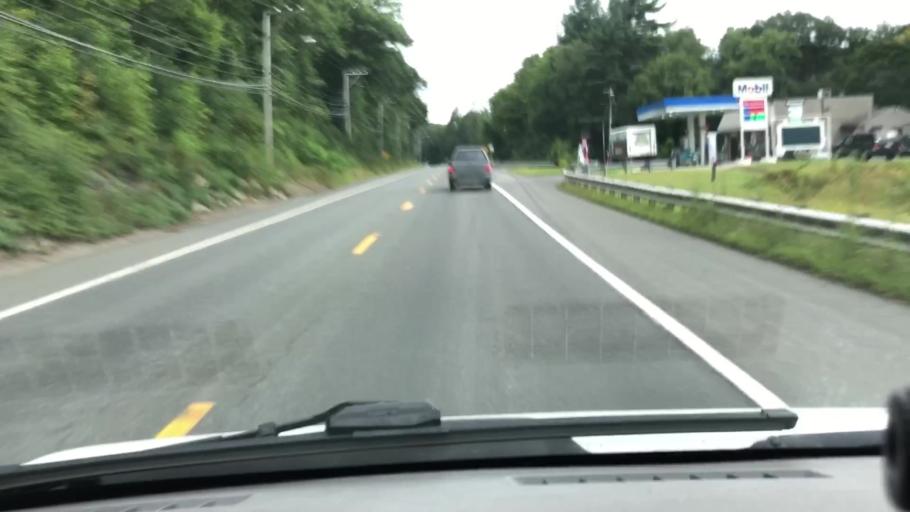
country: US
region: Massachusetts
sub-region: Franklin County
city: Shelburne Falls
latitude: 42.5977
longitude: -72.7289
